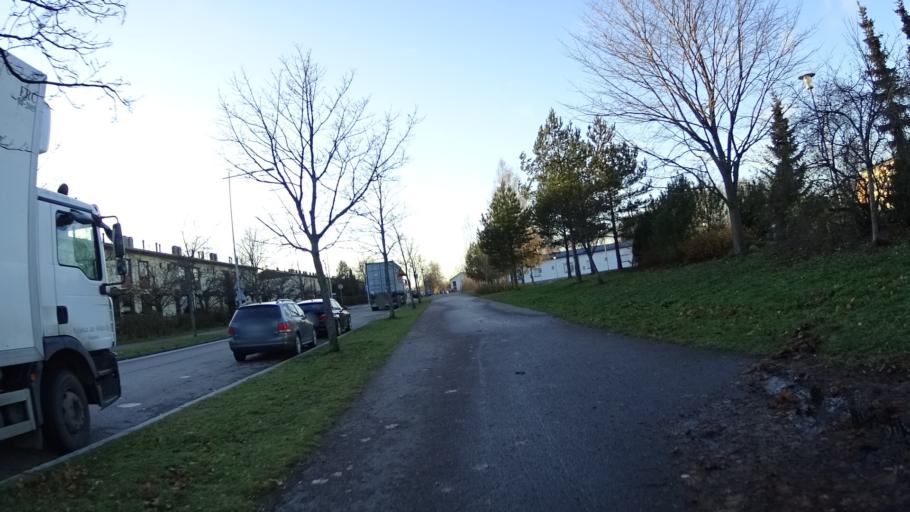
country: FI
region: Uusimaa
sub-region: Helsinki
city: Vantaa
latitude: 60.2975
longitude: 25.0286
